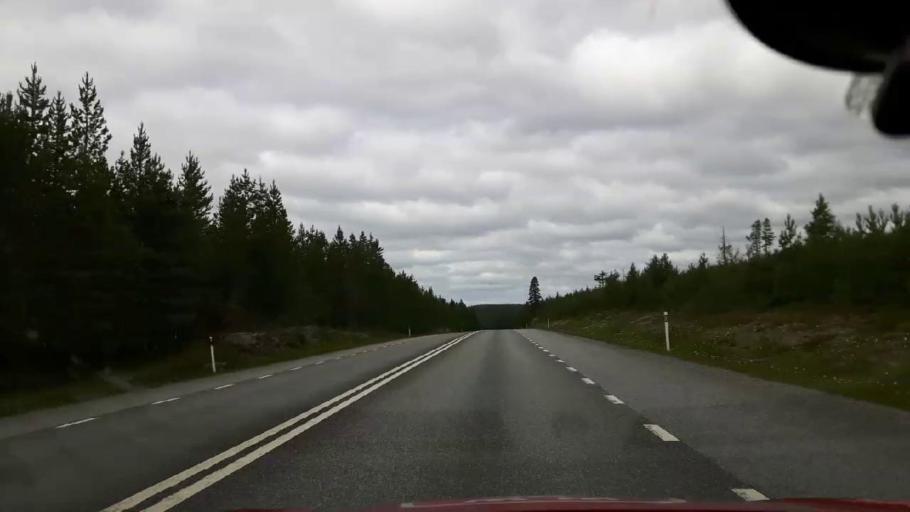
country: SE
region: Vaesternorrland
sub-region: Ange Kommun
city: Ange
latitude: 62.6810
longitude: 15.5893
